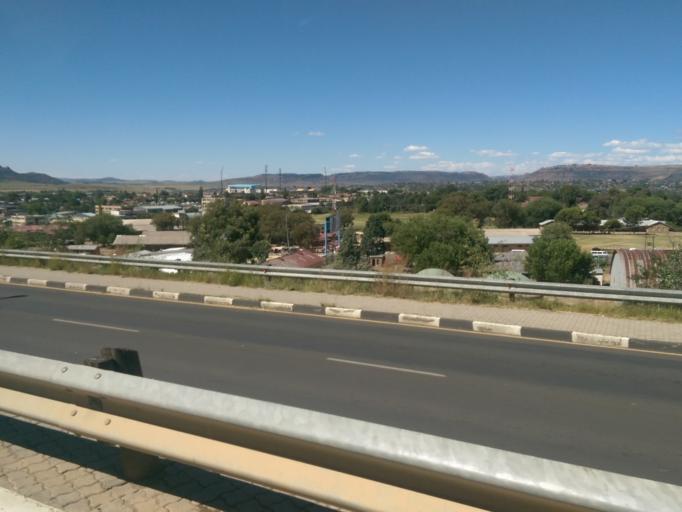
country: LS
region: Maseru
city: Maseru
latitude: -29.3200
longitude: 27.4943
